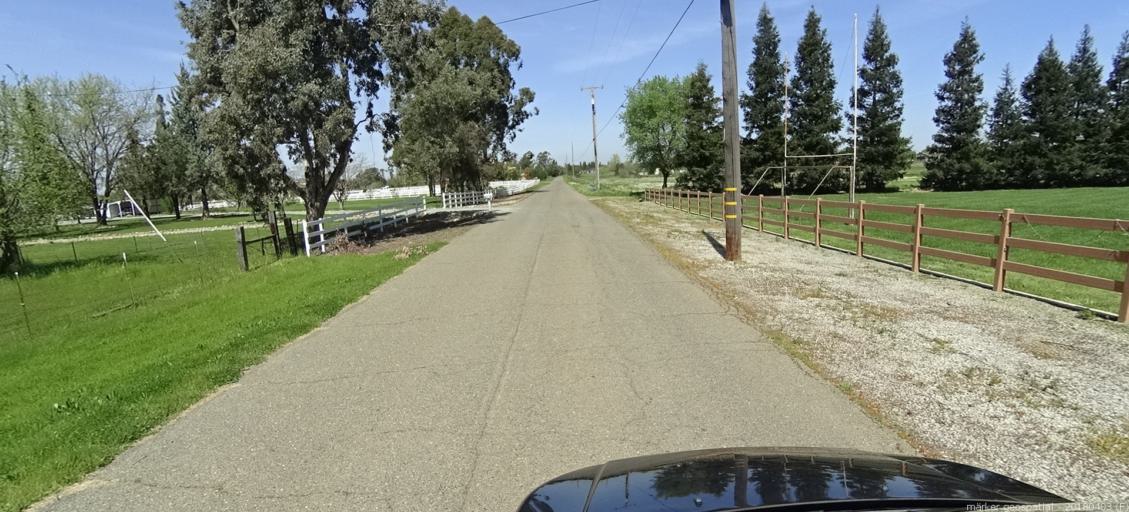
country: US
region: California
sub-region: Sacramento County
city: Wilton
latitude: 38.3883
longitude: -121.2468
